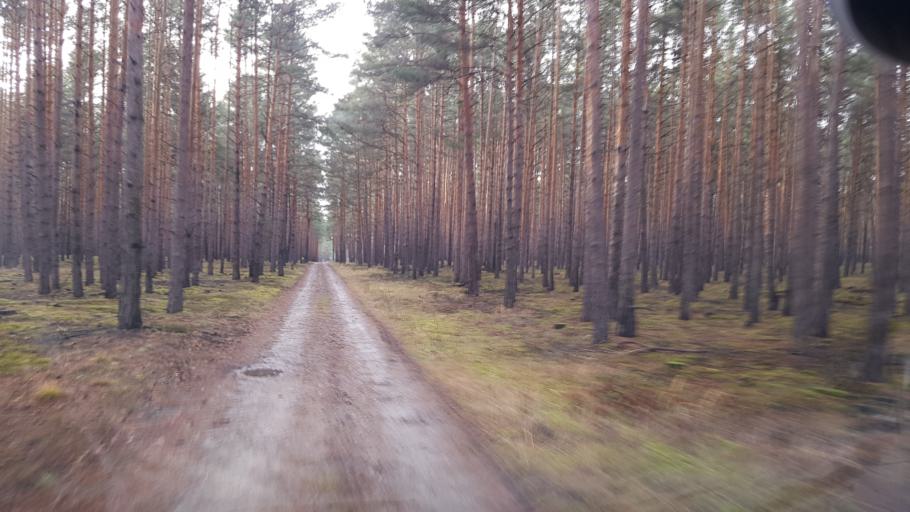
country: DE
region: Brandenburg
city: Sallgast
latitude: 51.6357
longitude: 13.8416
